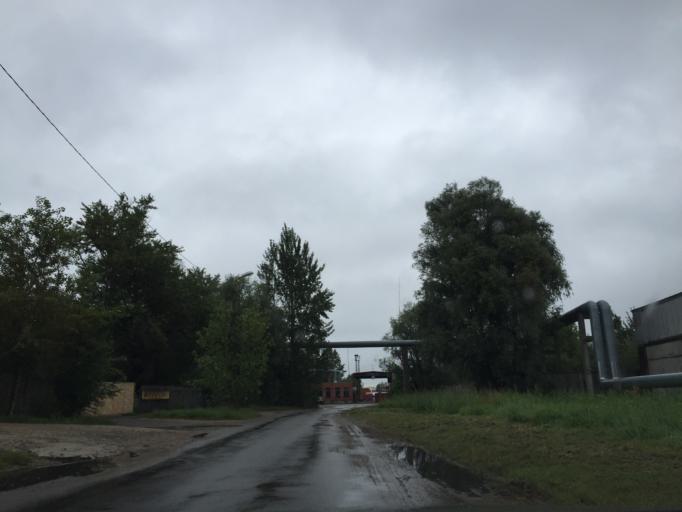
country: LV
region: Riga
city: Riga
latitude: 56.9833
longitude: 24.1123
